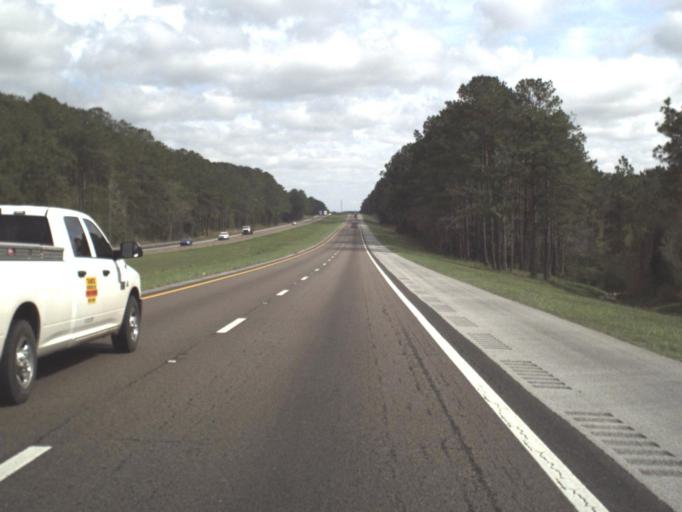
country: US
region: Florida
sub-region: Walton County
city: DeFuniak Springs
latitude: 30.7157
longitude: -86.1761
